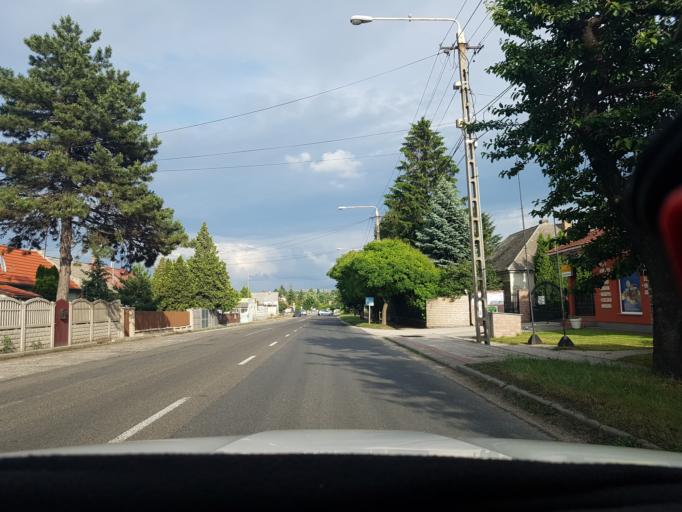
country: HU
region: Komarom-Esztergom
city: Labatlan
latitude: 47.7526
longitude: 18.4748
